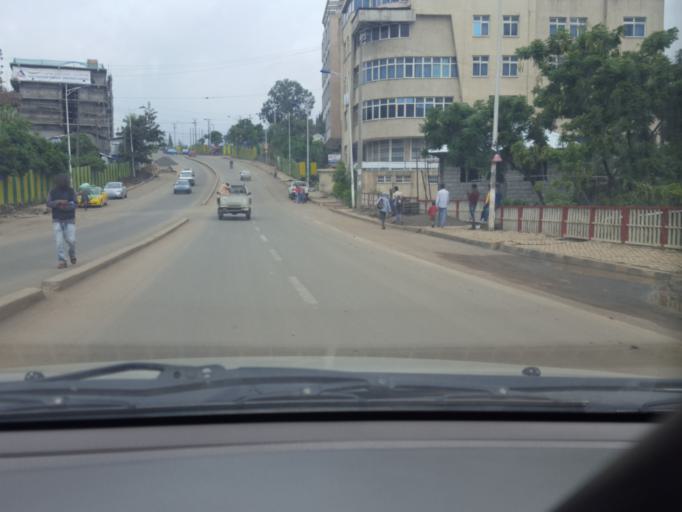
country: ET
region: Adis Abeba
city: Addis Ababa
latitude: 9.0287
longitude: 38.7590
